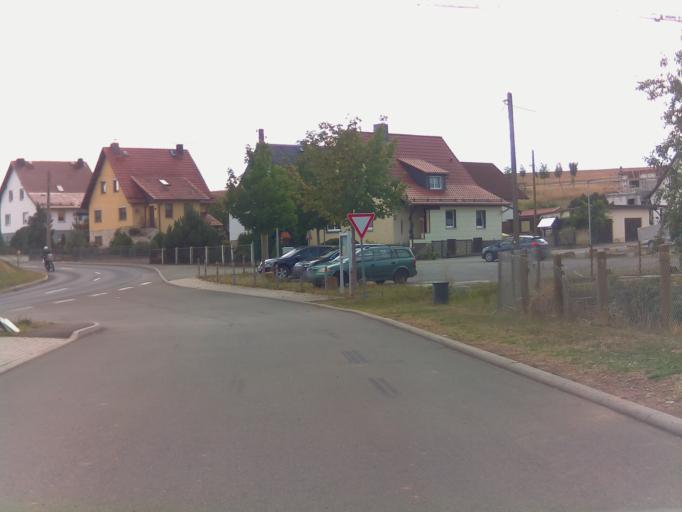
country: DE
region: Thuringia
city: Ritschenhausen
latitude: 50.5079
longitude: 10.4332
